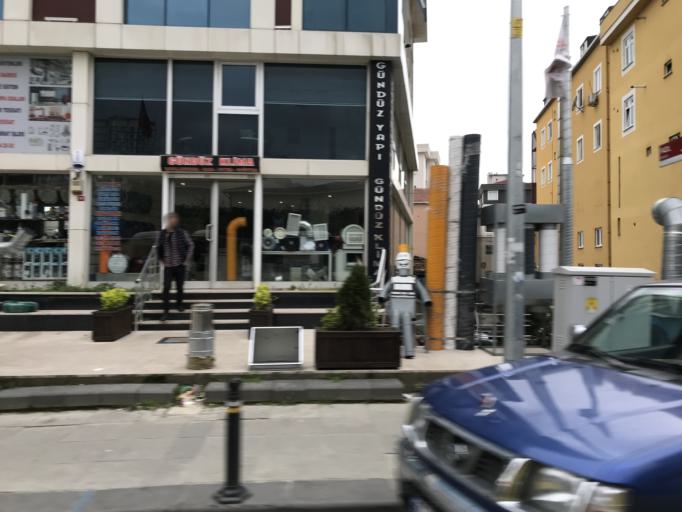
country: TR
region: Istanbul
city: Umraniye
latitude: 41.0097
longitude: 29.1716
